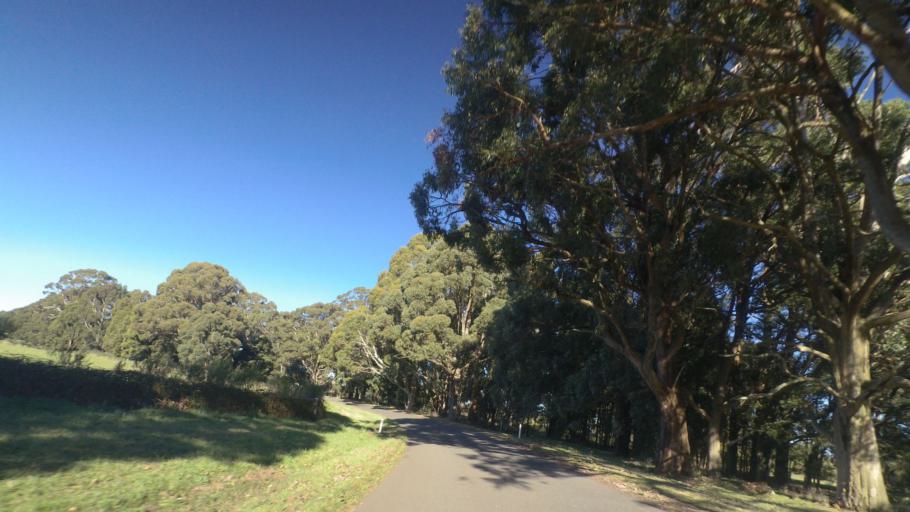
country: AU
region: Victoria
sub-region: Mount Alexander
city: Castlemaine
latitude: -37.3578
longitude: 144.2899
